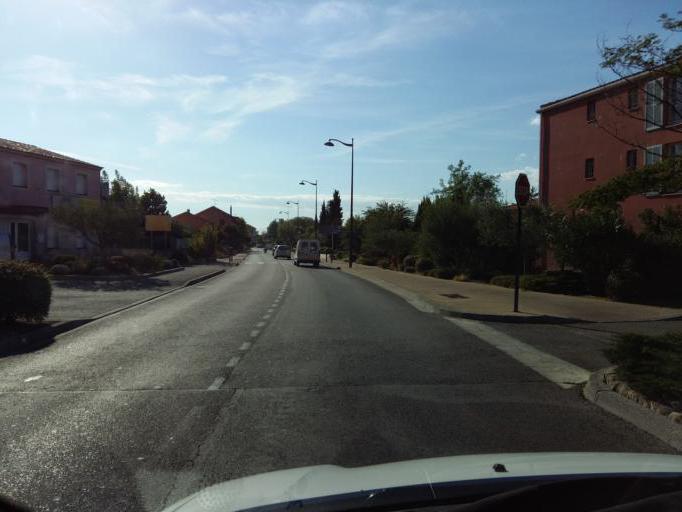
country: FR
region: Provence-Alpes-Cote d'Azur
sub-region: Departement du Vaucluse
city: Le Thor
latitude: 43.9274
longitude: 5.0023
